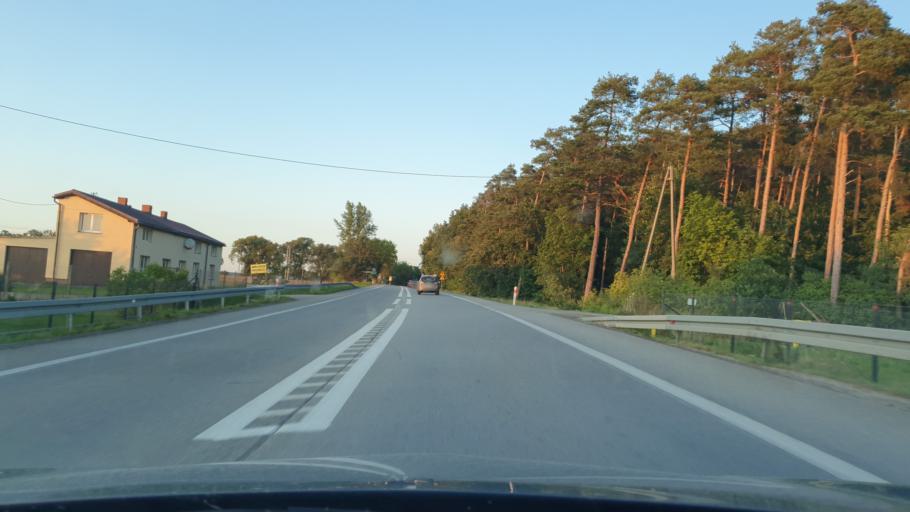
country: PL
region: Pomeranian Voivodeship
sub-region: Powiat leborski
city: Nowa Wies Leborska
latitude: 54.5095
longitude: 17.6681
